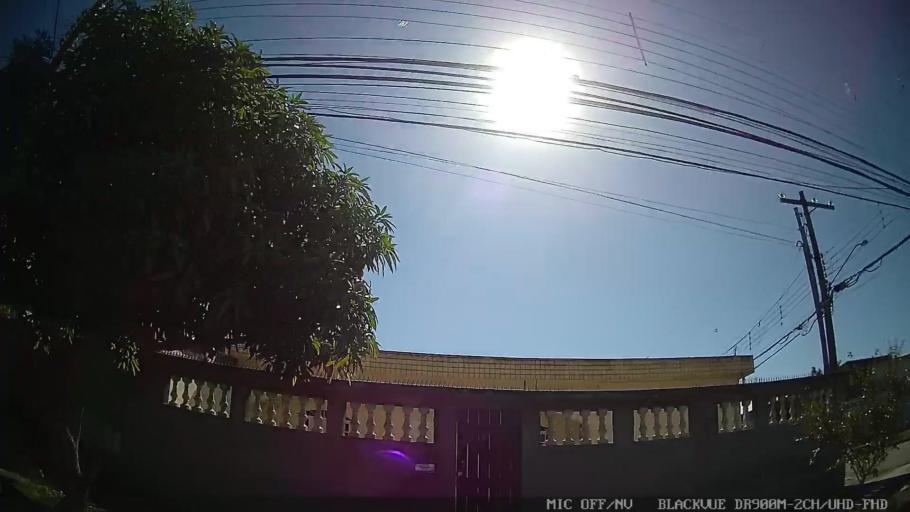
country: BR
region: Sao Paulo
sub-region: Guaruja
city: Guaruja
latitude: -23.9678
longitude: -46.2787
